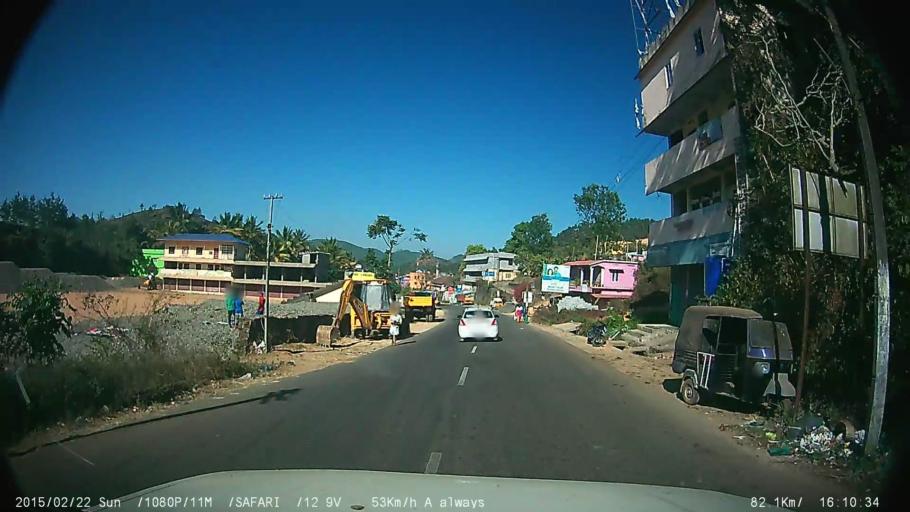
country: IN
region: Tamil Nadu
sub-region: Theni
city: Gudalur
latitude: 9.5699
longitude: 77.0873
